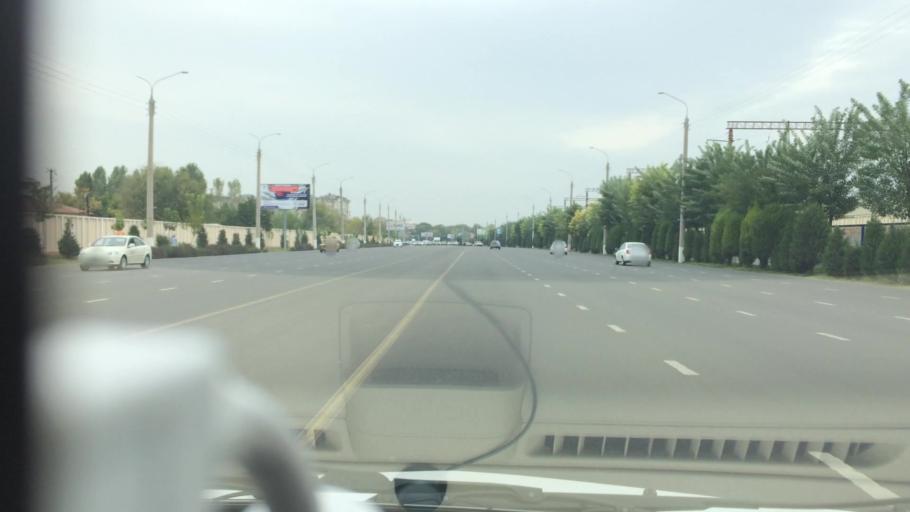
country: UZ
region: Toshkent Shahri
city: Tashkent
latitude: 41.2843
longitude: 69.2784
